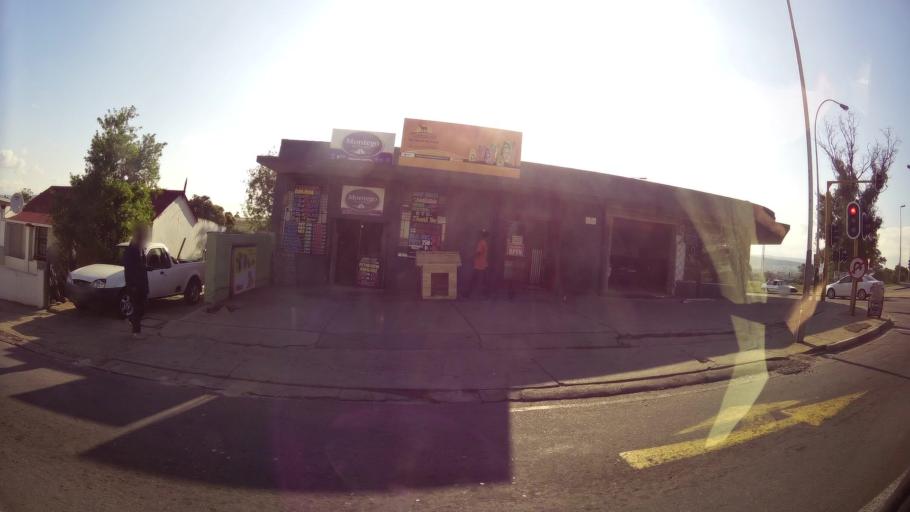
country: ZA
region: Eastern Cape
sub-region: Nelson Mandela Bay Metropolitan Municipality
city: Uitenhage
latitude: -33.7606
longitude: 25.3900
